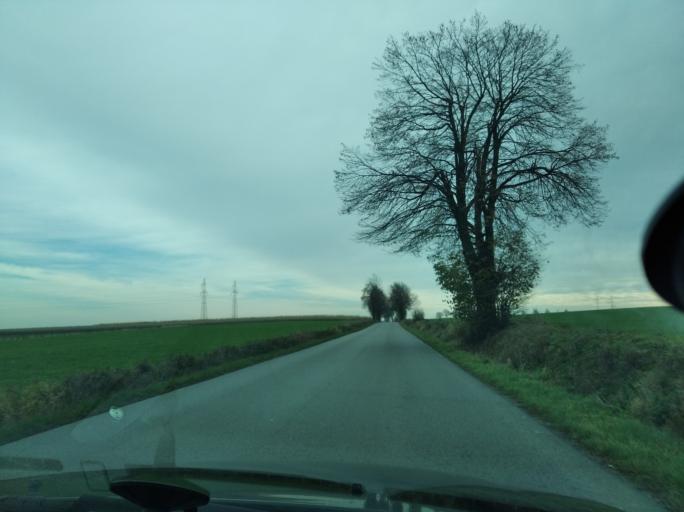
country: PL
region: Subcarpathian Voivodeship
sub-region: Powiat lancucki
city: Wysoka
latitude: 50.0261
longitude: 22.2517
